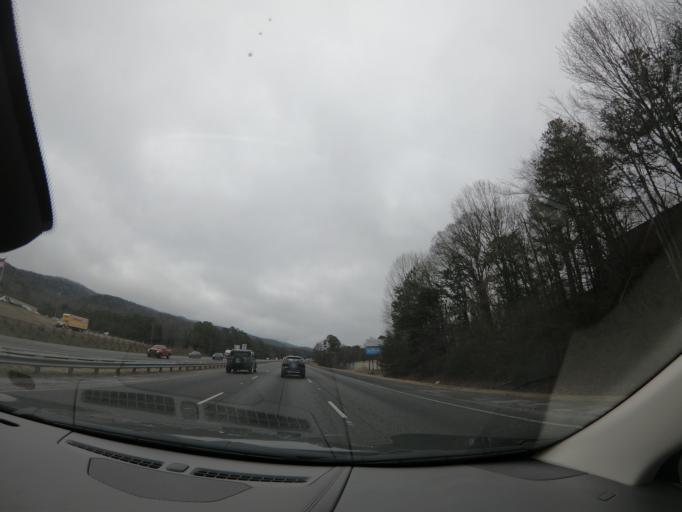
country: US
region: Georgia
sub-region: Whitfield County
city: Dalton
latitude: 34.7014
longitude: -85.0058
